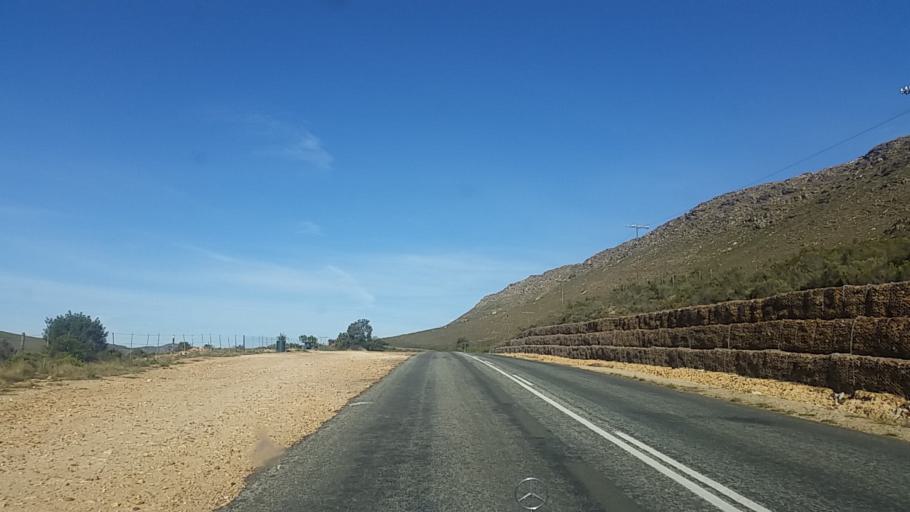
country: ZA
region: Western Cape
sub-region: Eden District Municipality
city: Knysna
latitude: -33.7426
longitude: 23.0150
